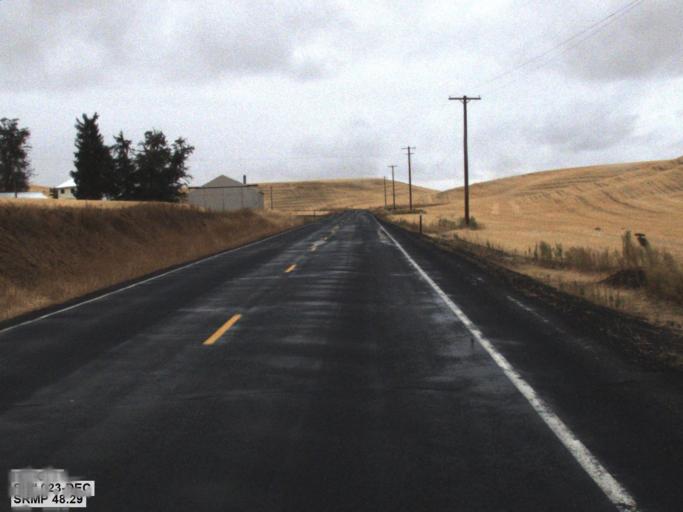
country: US
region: Washington
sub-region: Lincoln County
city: Davenport
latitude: 47.3507
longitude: -118.0272
